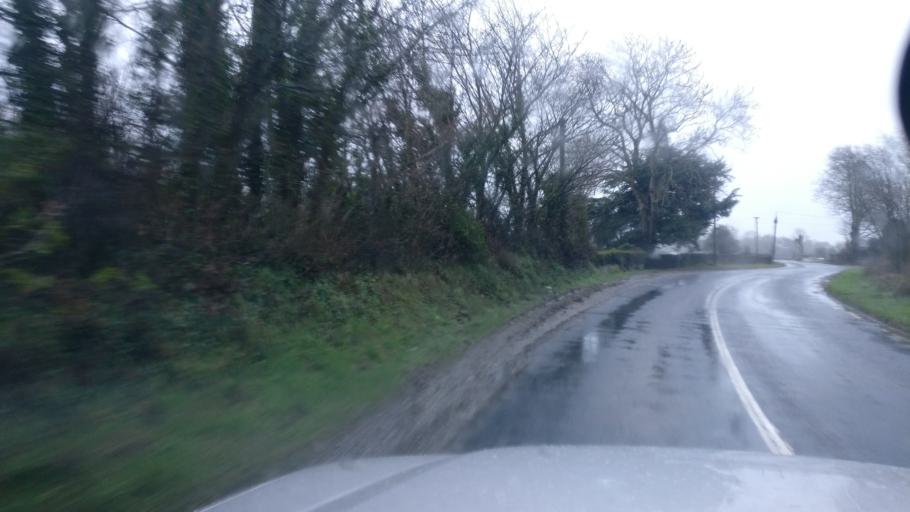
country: IE
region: Connaught
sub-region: County Galway
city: Ballinasloe
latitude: 53.2804
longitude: -8.2238
